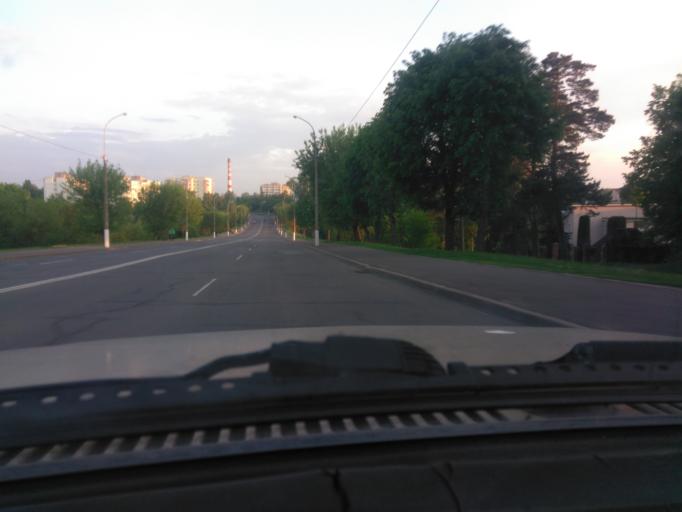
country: BY
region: Mogilev
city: Mahilyow
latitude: 53.9247
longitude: 30.3120
